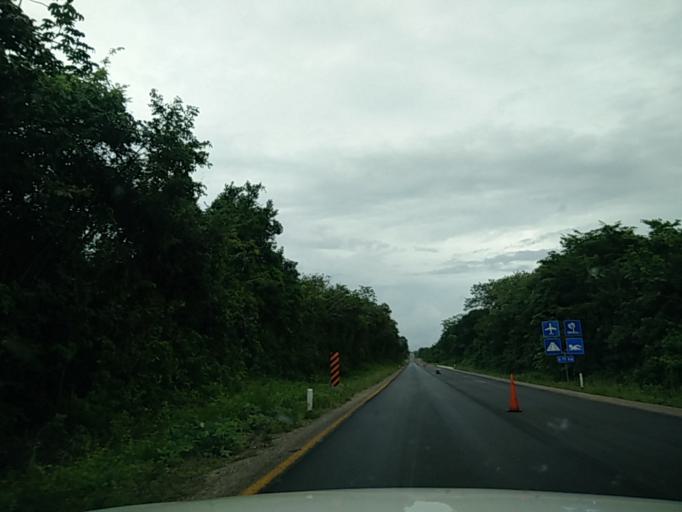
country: MX
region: Quintana Roo
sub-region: Lazaro Cardenas
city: El Tintal
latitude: 20.8985
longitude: -87.4784
